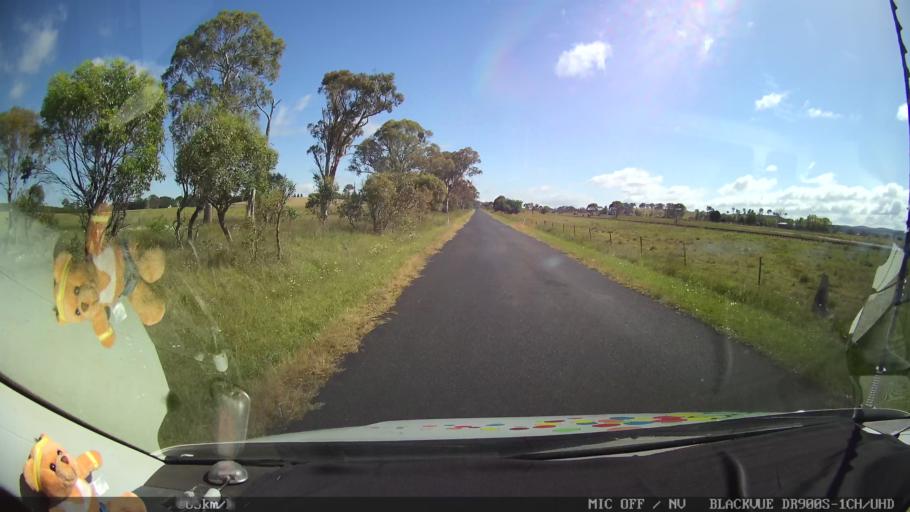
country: AU
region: New South Wales
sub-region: Guyra
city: Guyra
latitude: -30.1806
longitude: 151.6809
